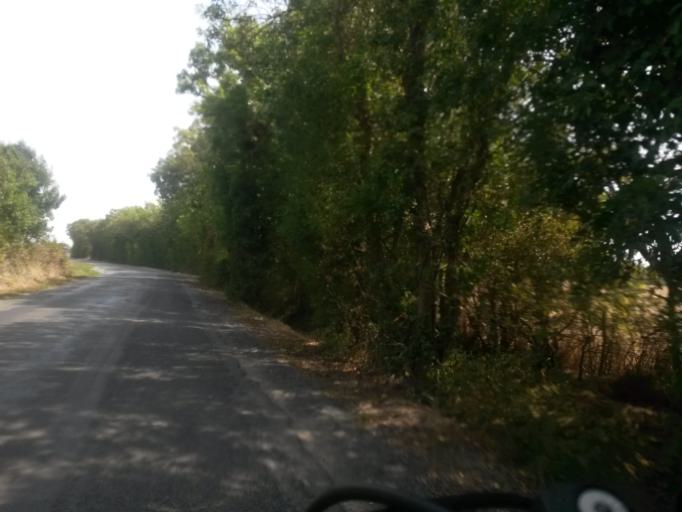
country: FR
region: Poitou-Charentes
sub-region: Departement de la Charente-Maritime
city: Nieul-sur-Mer
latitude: 46.2052
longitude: -1.1508
